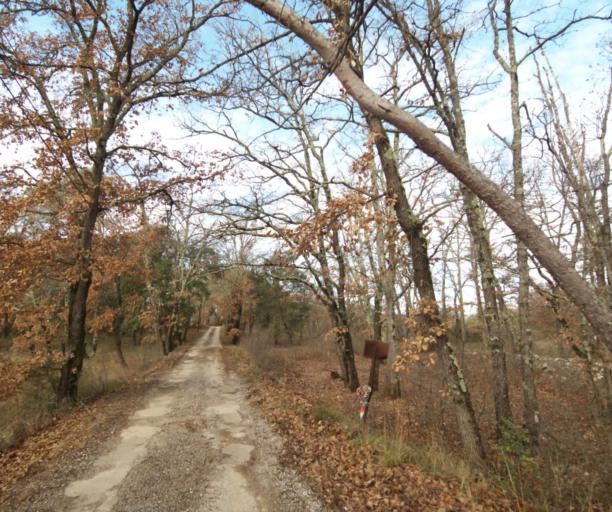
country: FR
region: Provence-Alpes-Cote d'Azur
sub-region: Departement du Var
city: Trans-en-Provence
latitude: 43.4953
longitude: 6.4594
